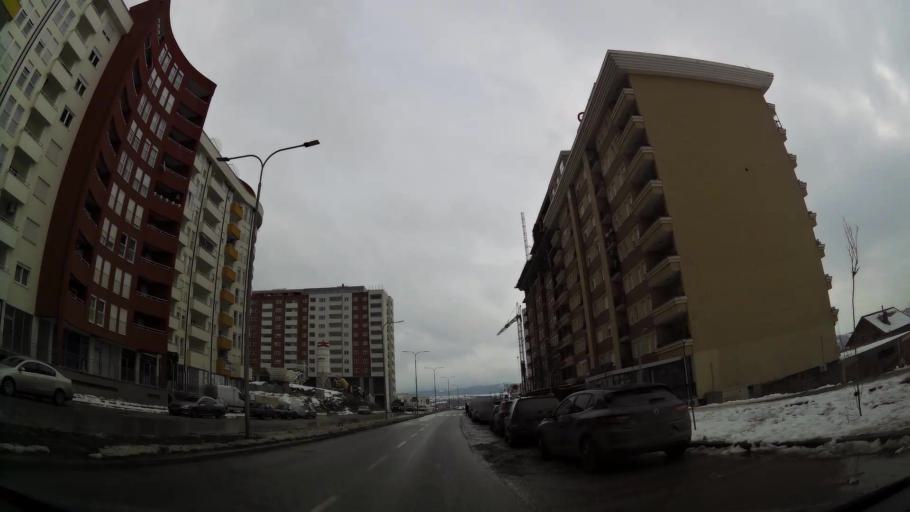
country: XK
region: Pristina
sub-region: Komuna e Prishtines
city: Pristina
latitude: 42.6492
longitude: 21.1806
